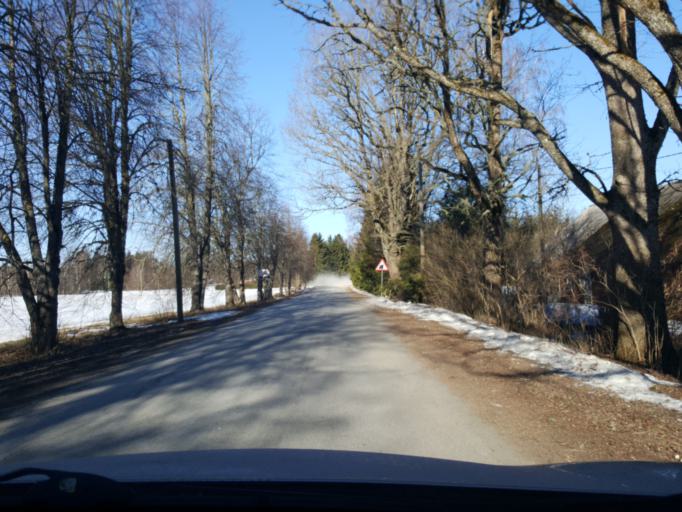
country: EE
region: Viljandimaa
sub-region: Viljandi linn
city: Viljandi
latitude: 58.4241
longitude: 25.5349
